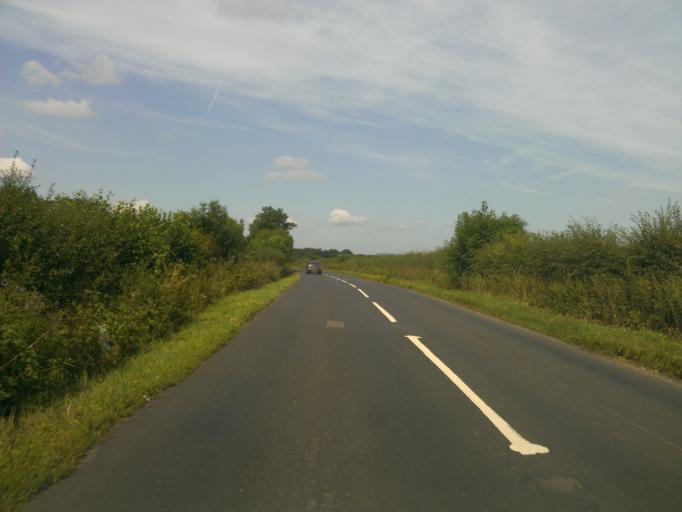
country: GB
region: England
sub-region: Kent
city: Sevenoaks
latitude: 51.1979
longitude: 0.1850
